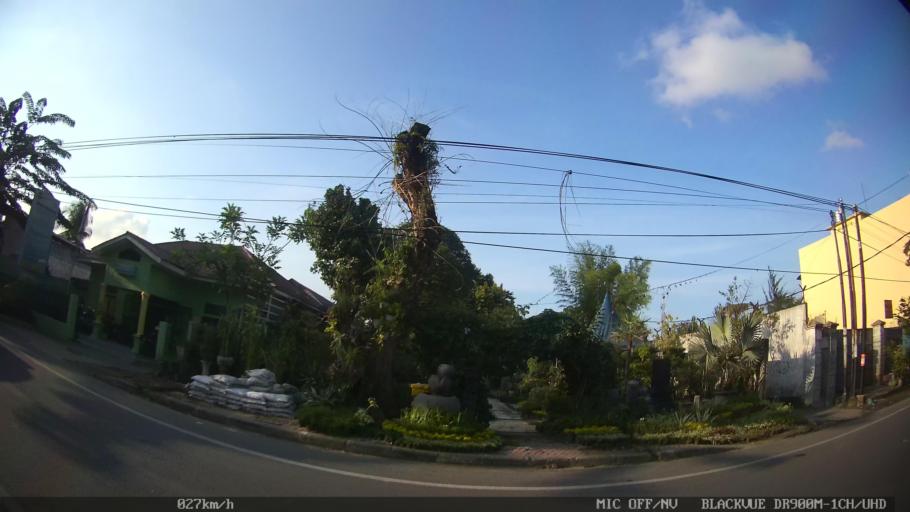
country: ID
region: North Sumatra
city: Medan
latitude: 3.6072
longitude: 98.6666
